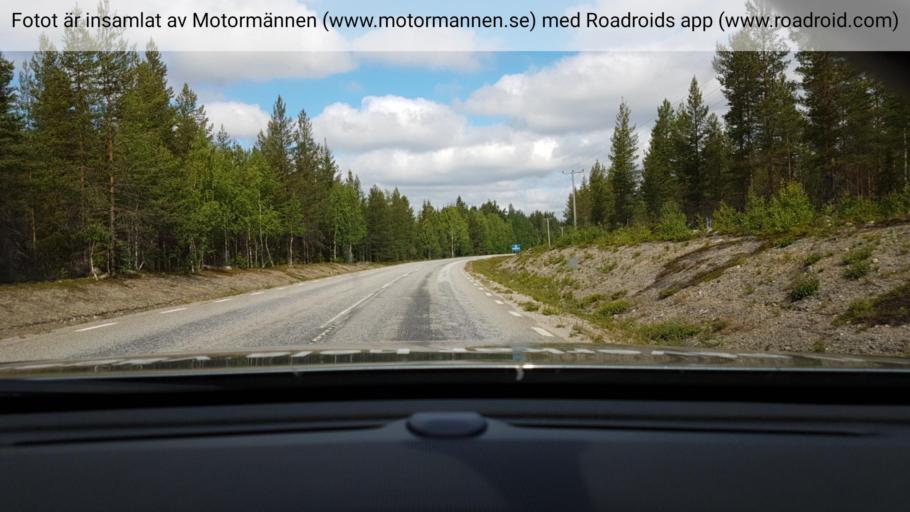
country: SE
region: Vaesterbotten
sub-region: Lycksele Kommun
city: Lycksele
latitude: 64.8598
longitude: 18.7265
